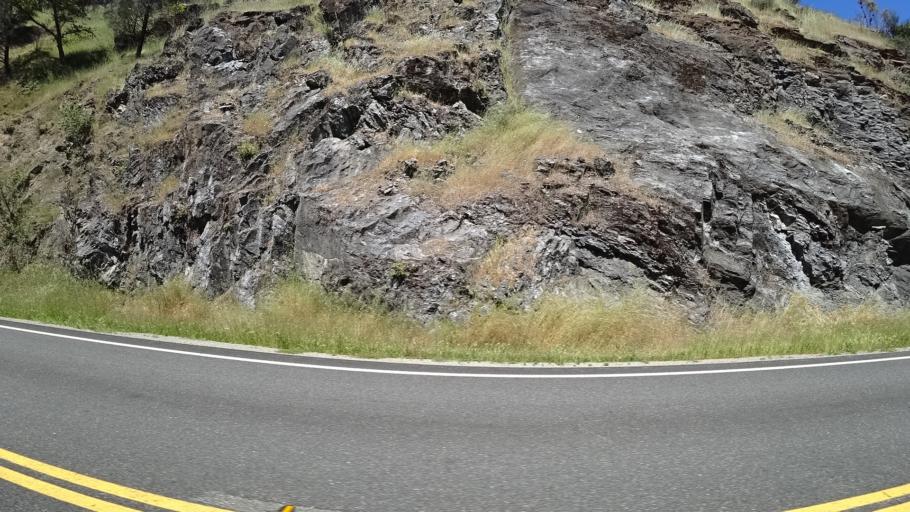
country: US
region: California
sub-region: Trinity County
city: Weaverville
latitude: 40.7663
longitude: -123.1050
